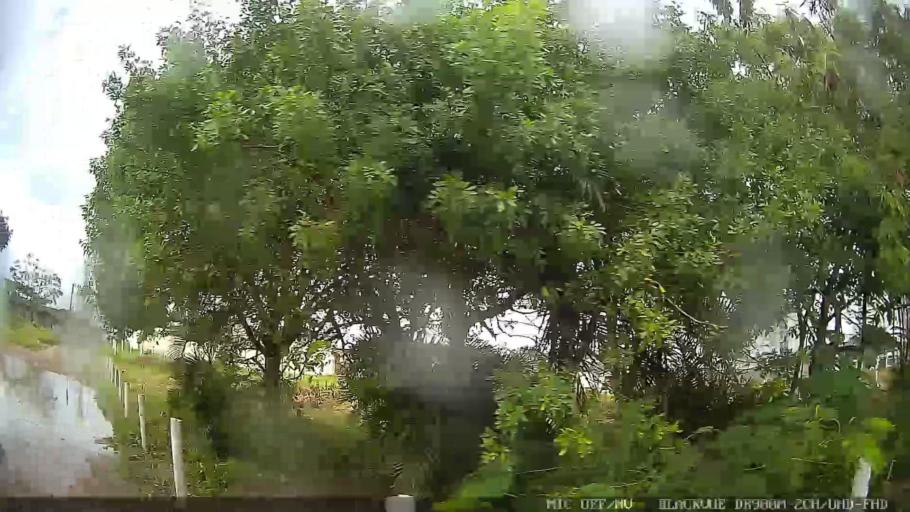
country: BR
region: Sao Paulo
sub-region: Itanhaem
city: Itanhaem
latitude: -24.1719
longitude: -46.7690
